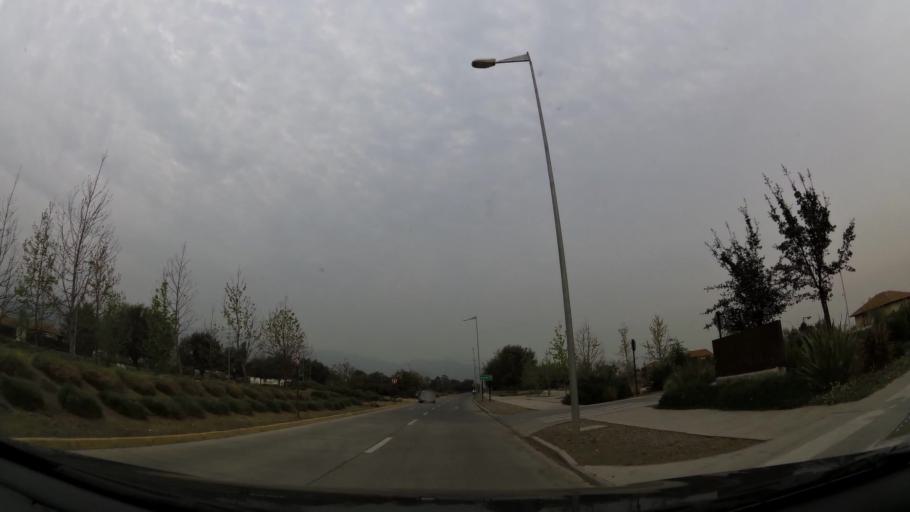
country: CL
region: Santiago Metropolitan
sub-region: Provincia de Chacabuco
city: Chicureo Abajo
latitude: -33.2568
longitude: -70.6278
